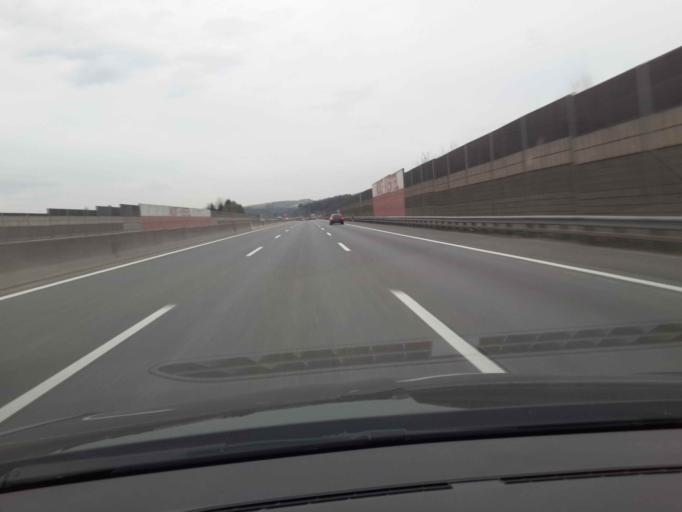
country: AT
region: Lower Austria
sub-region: Politischer Bezirk Melk
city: Blindenmarkt
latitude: 48.1313
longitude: 14.9980
